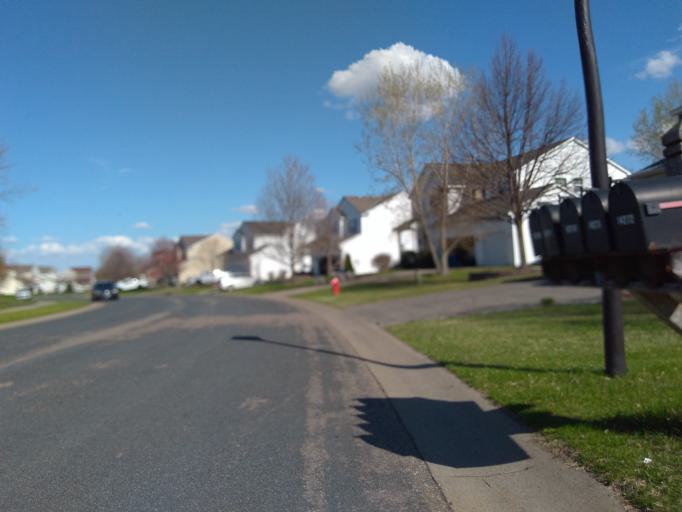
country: US
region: Minnesota
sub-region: Dakota County
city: Rosemount
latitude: 44.7400
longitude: -93.1065
